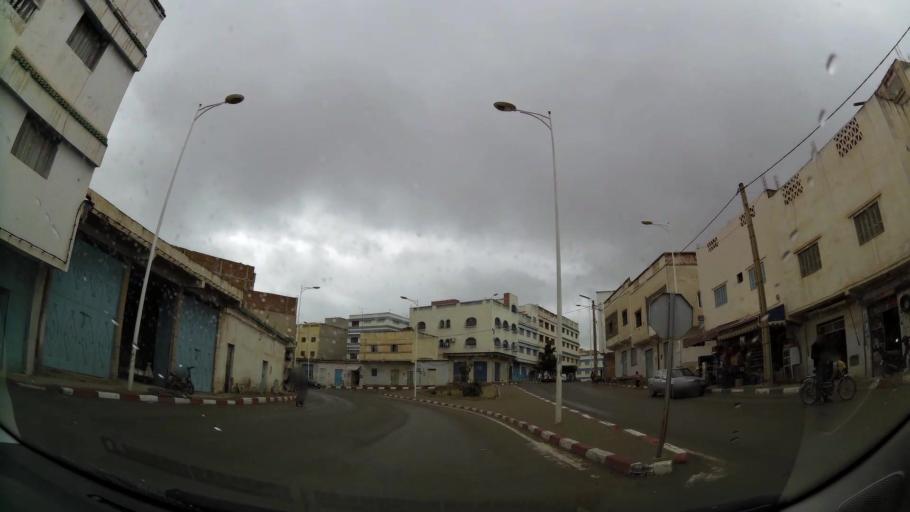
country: MA
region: Oriental
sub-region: Nador
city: Midar
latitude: 35.0473
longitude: -3.4524
